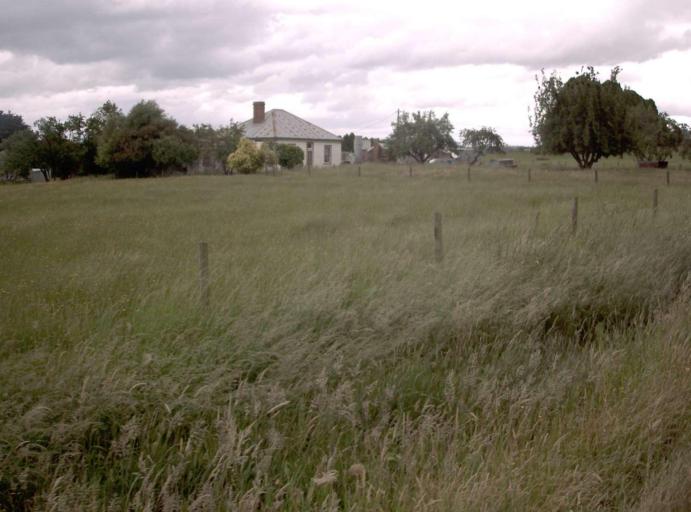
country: AU
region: Victoria
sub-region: Baw Baw
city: Warragul
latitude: -38.1530
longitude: 145.9847
